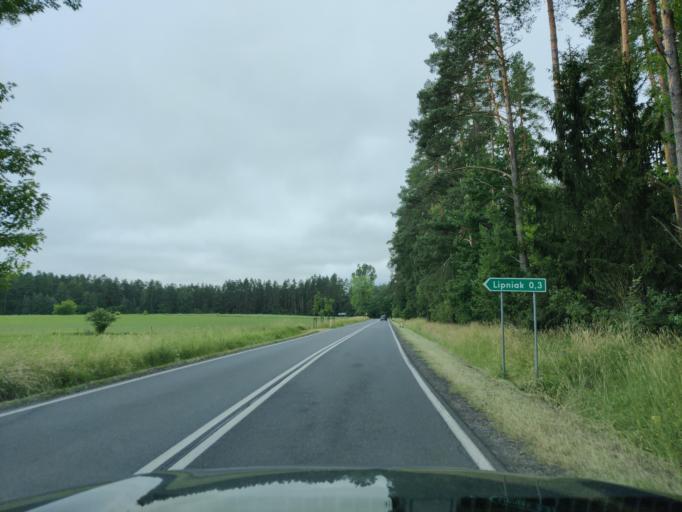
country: PL
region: Warmian-Masurian Voivodeship
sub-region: Powiat szczycienski
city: Rozogi
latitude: 53.5092
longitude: 21.3750
